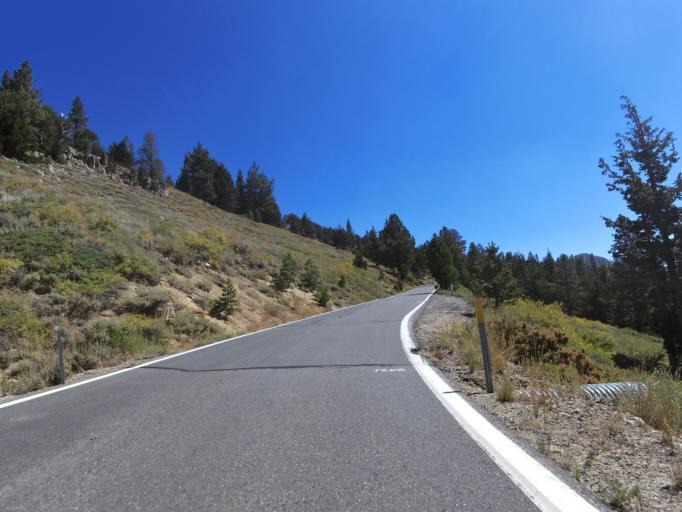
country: US
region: Nevada
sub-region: Douglas County
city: Gardnerville Ranchos
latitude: 38.5465
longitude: -119.8283
